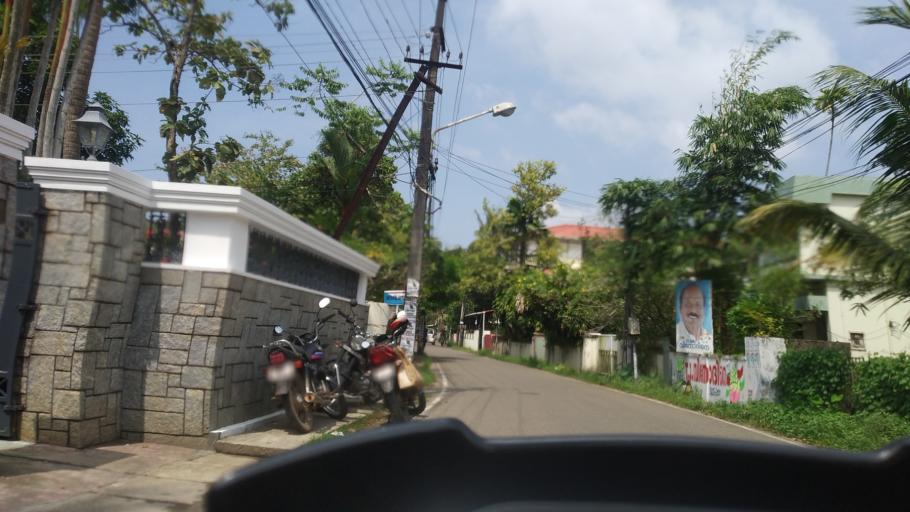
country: IN
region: Kerala
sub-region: Ernakulam
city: Cochin
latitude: 9.9873
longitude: 76.2980
